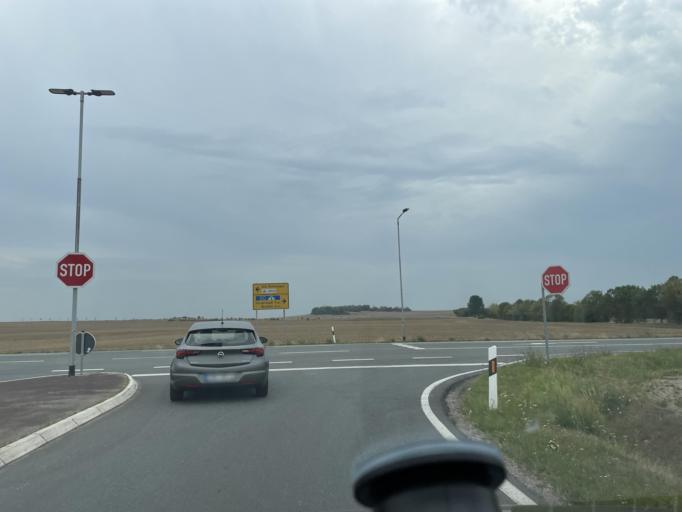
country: DE
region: Saxony-Anhalt
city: Calbe
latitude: 51.8967
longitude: 11.7537
